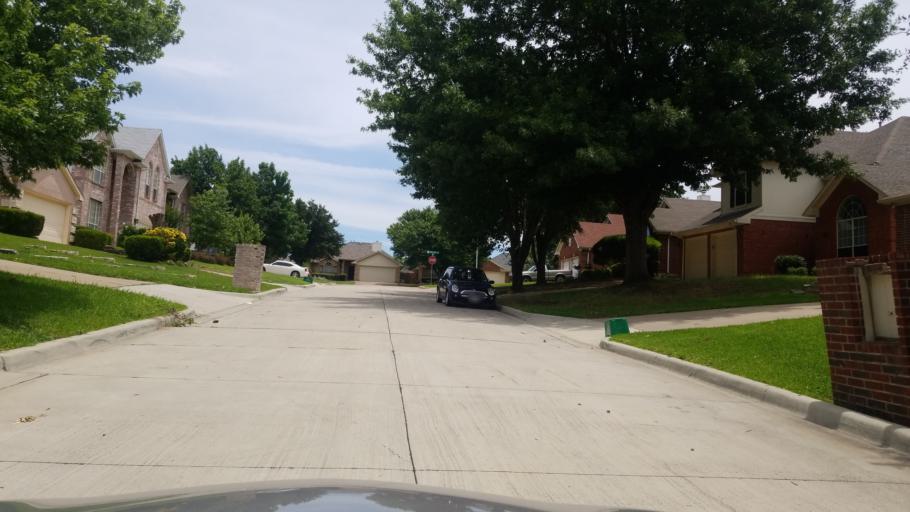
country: US
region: Texas
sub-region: Dallas County
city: Grand Prairie
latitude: 32.6788
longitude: -96.9918
